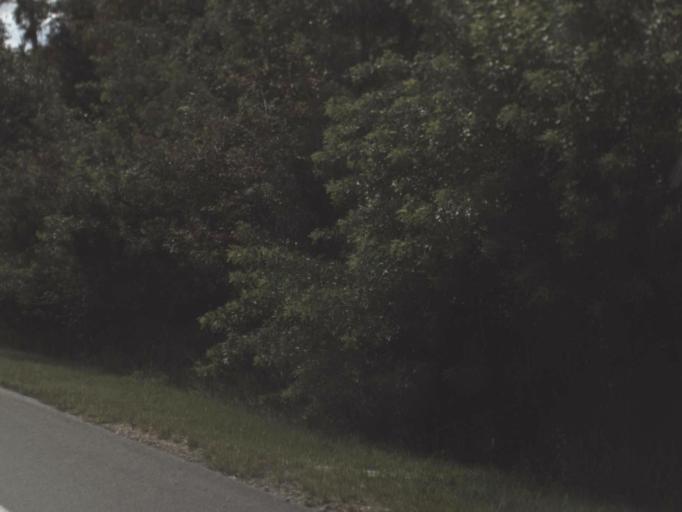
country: US
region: Florida
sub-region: Collier County
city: Lely Resort
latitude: 25.9381
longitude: -81.3572
